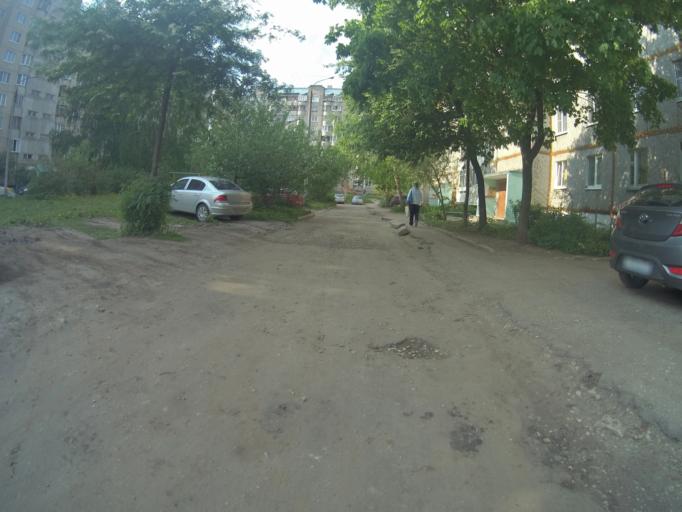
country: RU
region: Vladimir
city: Kommunar
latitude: 56.1662
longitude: 40.4472
